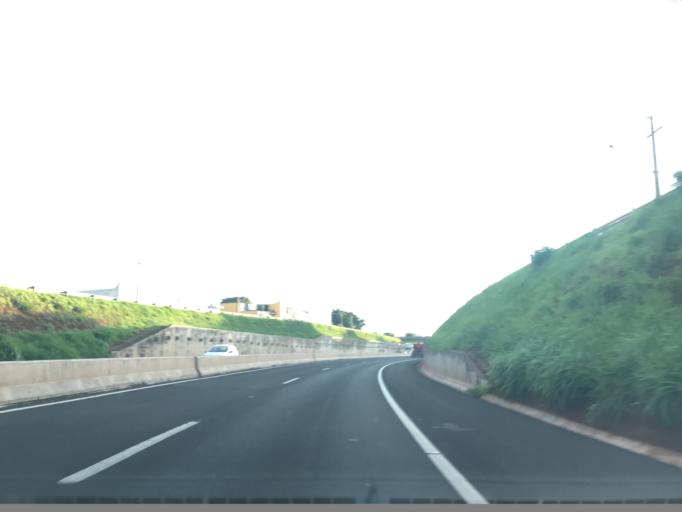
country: BR
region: Parana
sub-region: Maringa
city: Maringa
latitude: -23.3814
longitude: -51.9610
